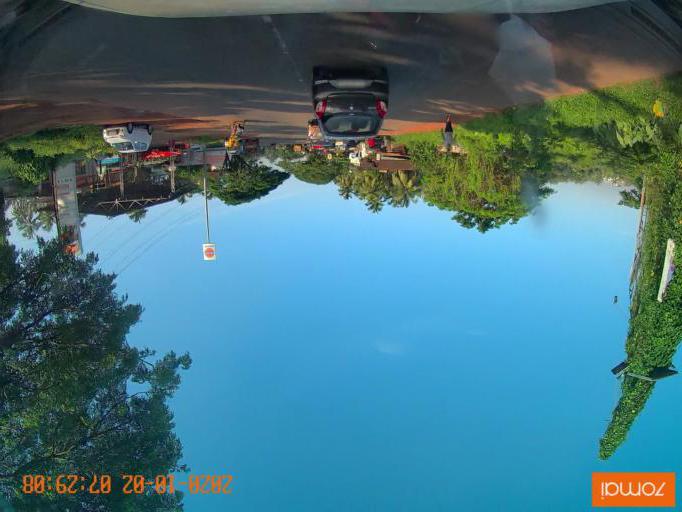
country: IN
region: Kerala
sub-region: Malappuram
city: Pariyapuram
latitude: 11.0325
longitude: 75.9400
